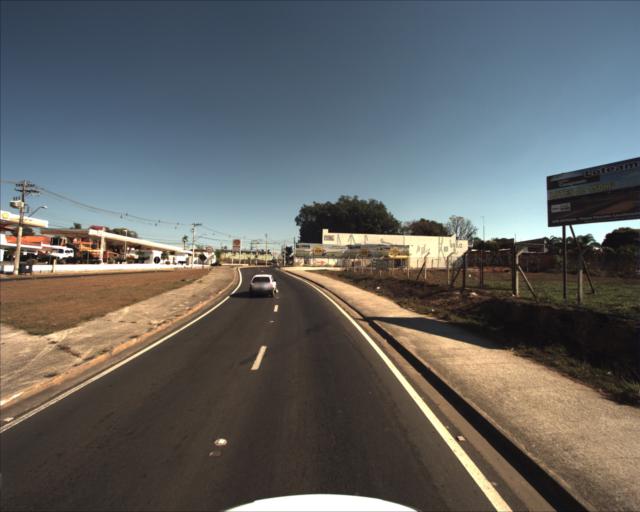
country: BR
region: Sao Paulo
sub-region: Sorocaba
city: Sorocaba
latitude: -23.4169
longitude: -47.4076
